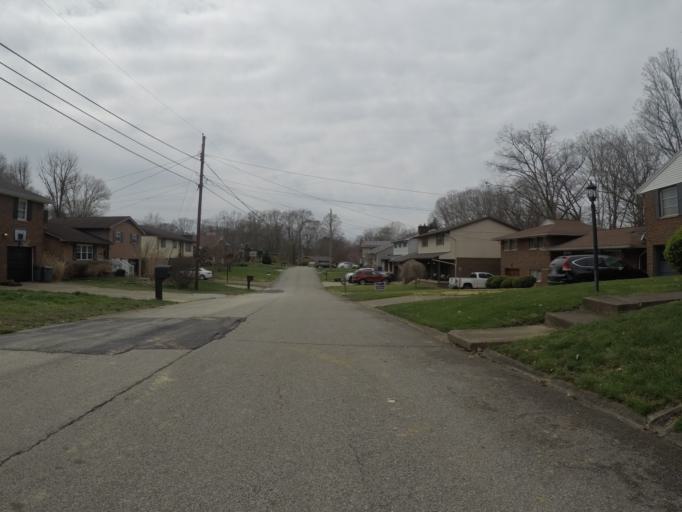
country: US
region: West Virginia
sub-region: Cabell County
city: Pea Ridge
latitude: 38.4213
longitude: -82.3225
